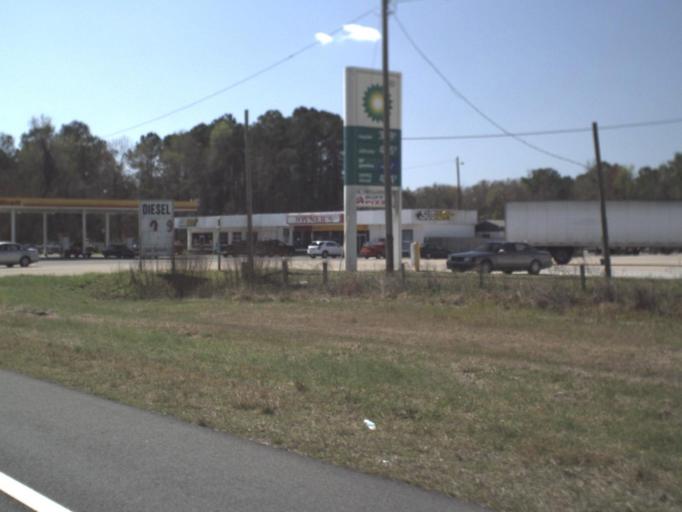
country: US
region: Florida
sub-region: Jefferson County
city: Monticello
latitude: 30.4848
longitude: -84.0241
